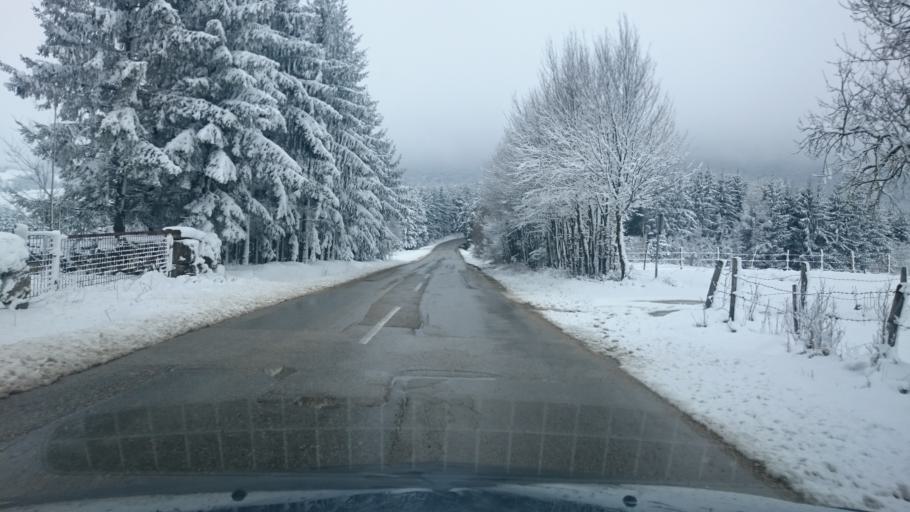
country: BA
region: Republika Srpska
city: Skender Vakuf
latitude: 44.4964
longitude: 17.3329
